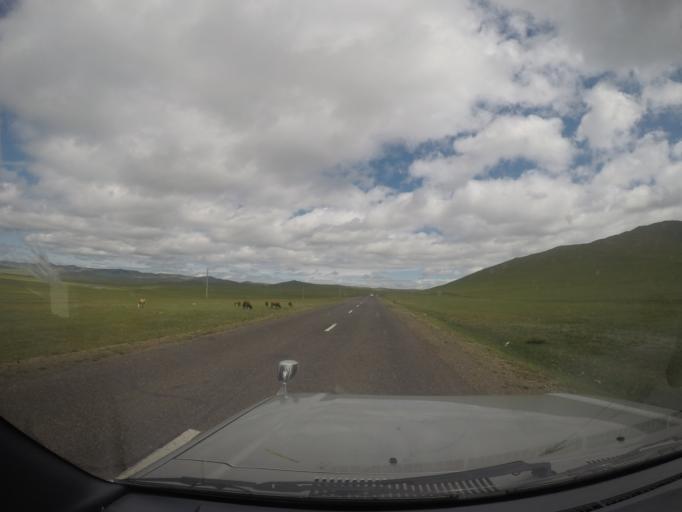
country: MN
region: Hentiy
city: Modot
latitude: 47.7607
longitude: 108.9264
